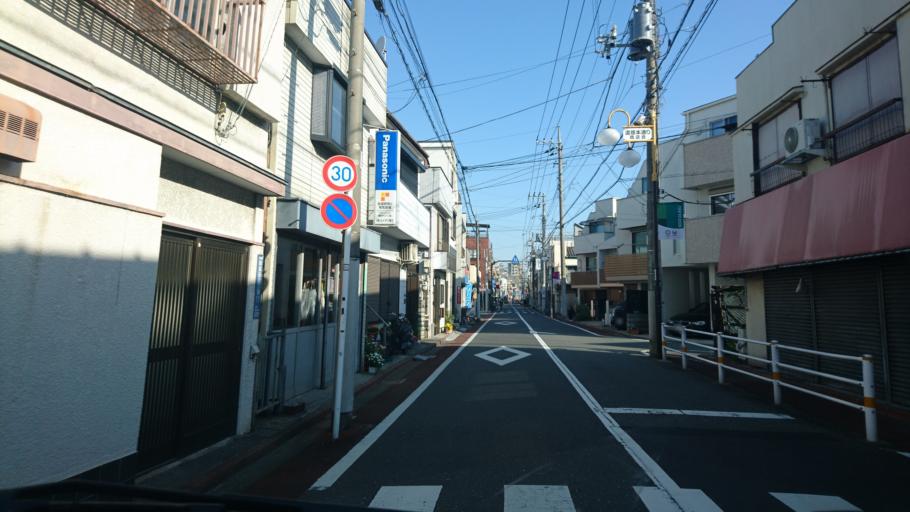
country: JP
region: Kanagawa
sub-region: Kawasaki-shi
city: Kawasaki
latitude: 35.5570
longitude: 139.7090
